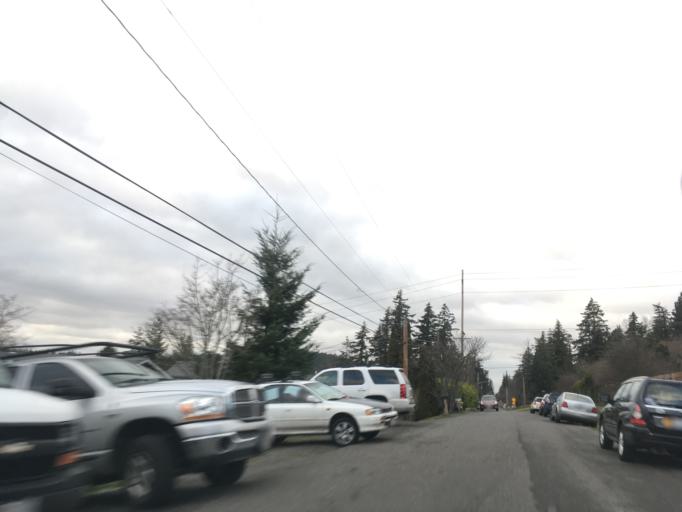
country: US
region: Washington
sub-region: Whatcom County
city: Bellingham
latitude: 48.7161
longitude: -122.4726
